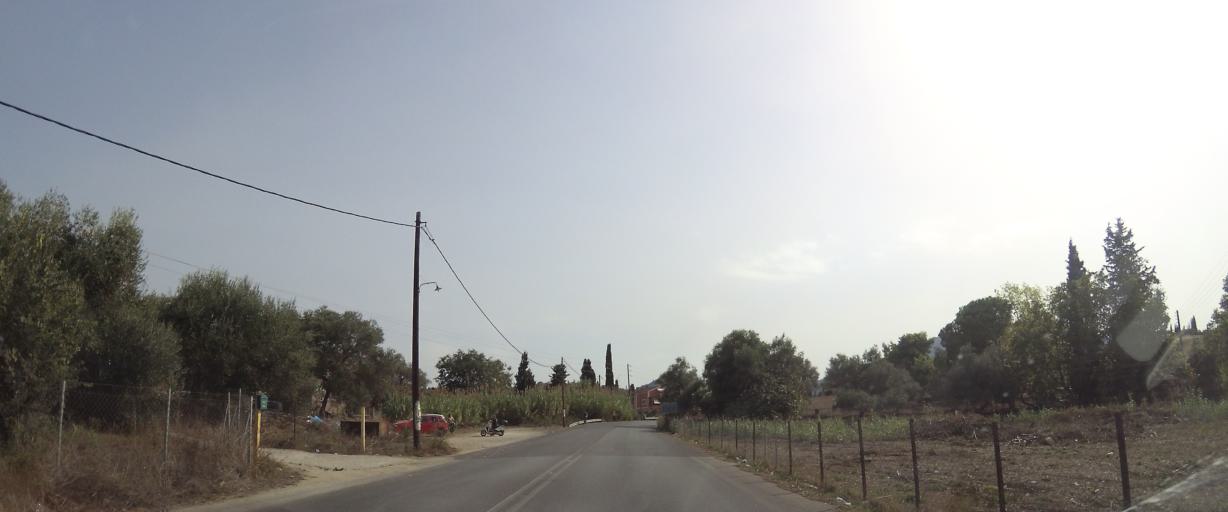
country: GR
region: Ionian Islands
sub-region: Nomos Kerkyras
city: Viros
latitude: 39.5846
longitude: 19.8931
